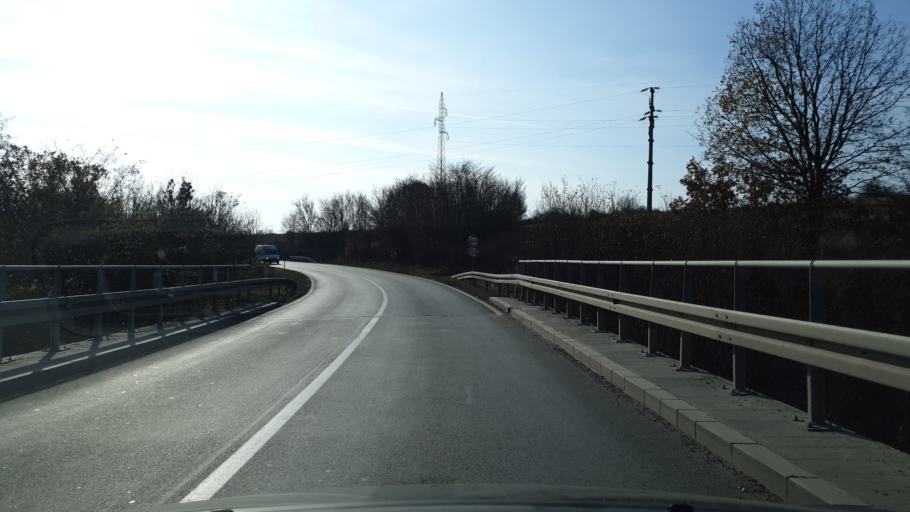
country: RS
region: Central Serbia
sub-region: Borski Okrug
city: Bor
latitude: 44.0467
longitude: 22.0980
